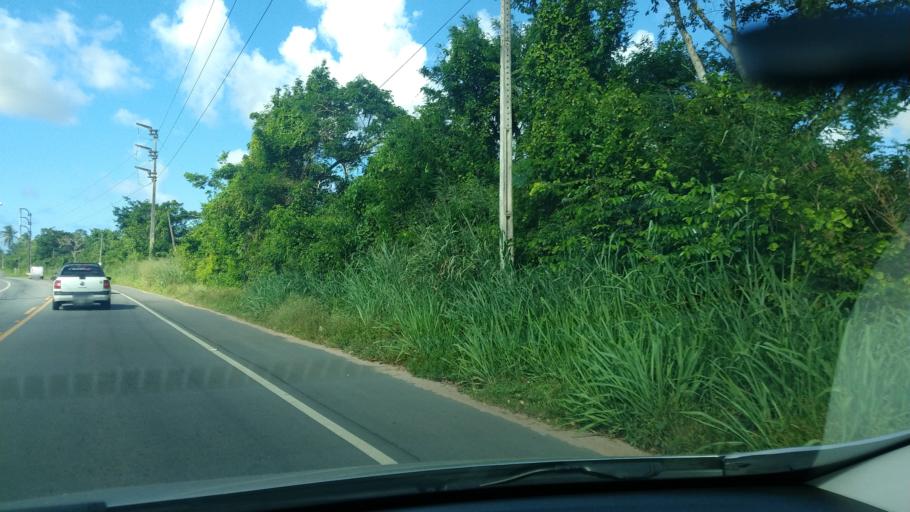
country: BR
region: Rio Grande do Norte
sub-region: Sao Goncalo Do Amarante
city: Sao Goncalo do Amarante
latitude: -5.7869
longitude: -35.2914
